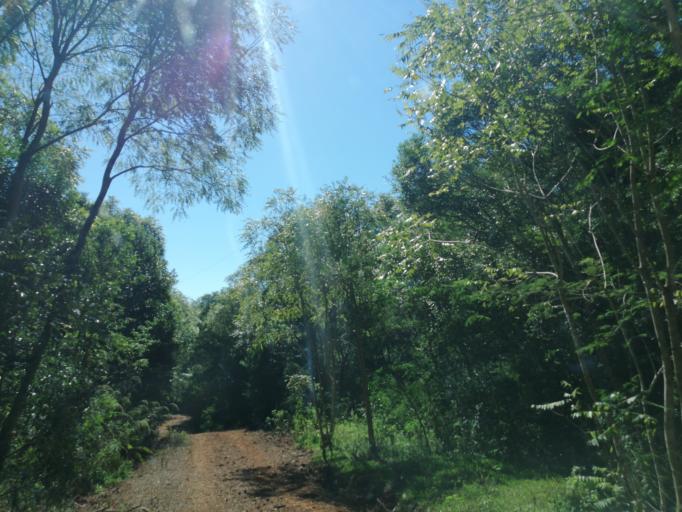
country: AR
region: Misiones
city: El Soberbio
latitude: -27.0634
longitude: -54.3748
